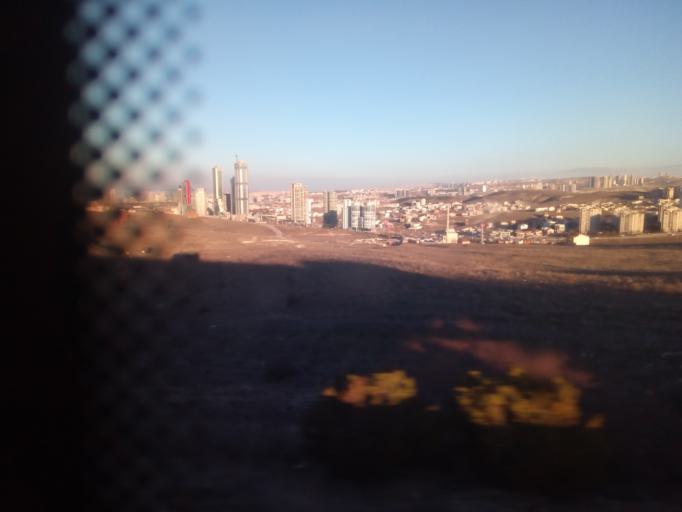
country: TR
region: Ankara
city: Etimesgut
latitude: 39.8720
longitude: 32.6339
